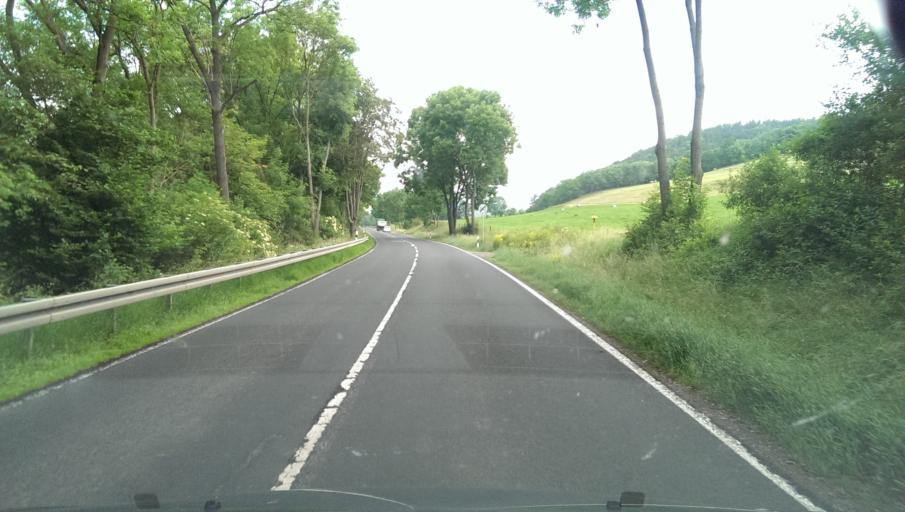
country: DE
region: Thuringia
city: Barchfeld
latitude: 50.8196
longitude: 11.1824
